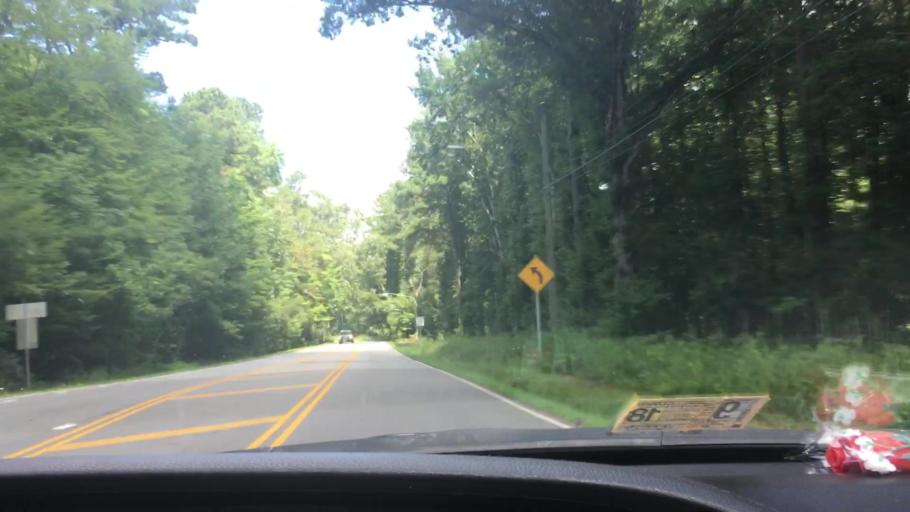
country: US
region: Virginia
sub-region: City of Virginia Beach
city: Virginia Beach
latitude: 36.7351
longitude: -76.0994
